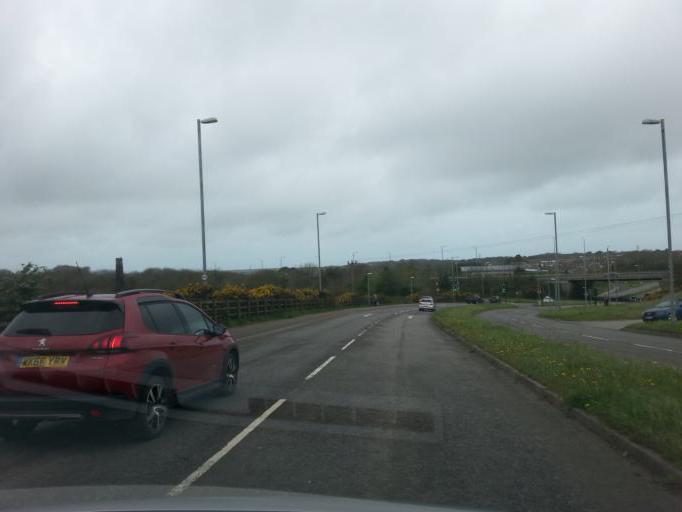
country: GB
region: England
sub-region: Cornwall
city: Camborne
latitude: 50.2275
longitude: -5.2815
